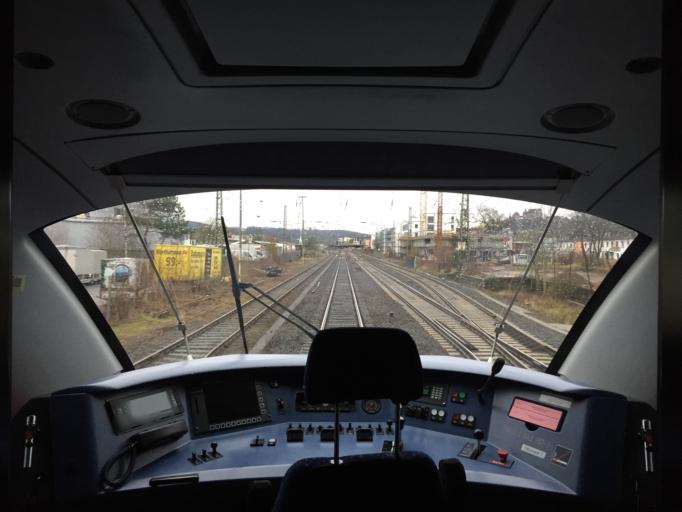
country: DE
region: Hesse
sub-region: Regierungsbezirk Giessen
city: Marburg an der Lahn
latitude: 50.8270
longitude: 8.7721
